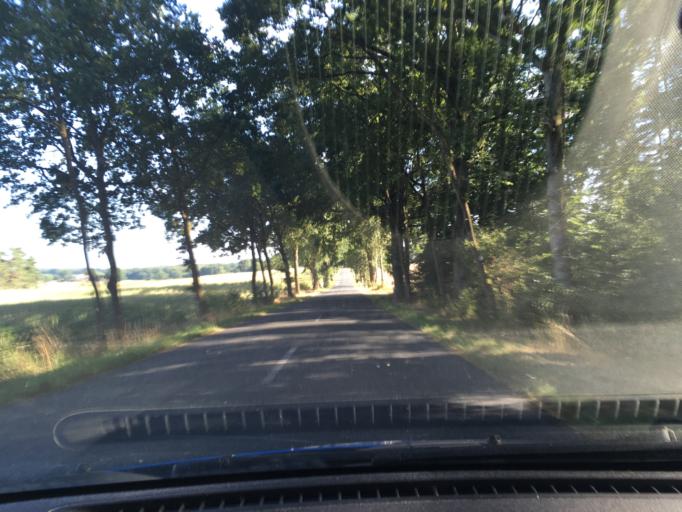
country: DE
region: Lower Saxony
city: Thomasburg
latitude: 53.2336
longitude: 10.7038
